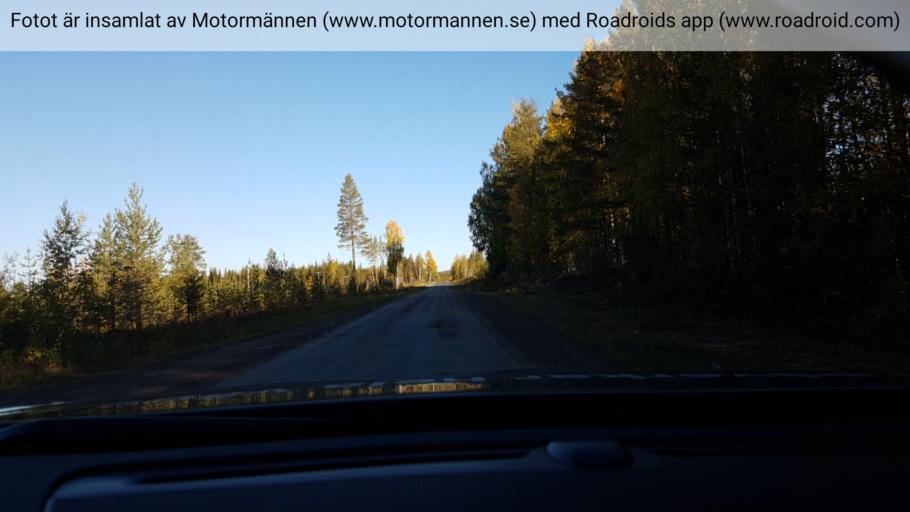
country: SE
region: Norrbotten
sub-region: Alvsbyns Kommun
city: AElvsbyn
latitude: 66.2236
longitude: 21.1621
